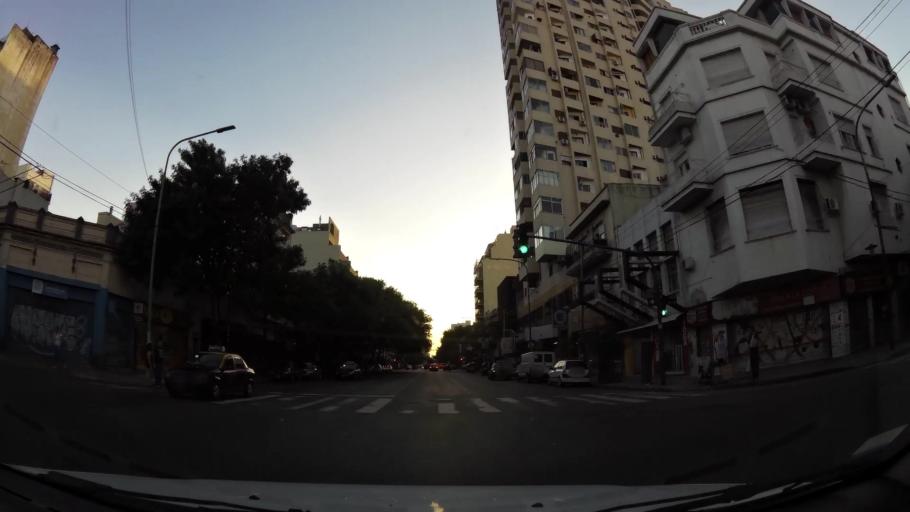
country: AR
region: Buenos Aires F.D.
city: Colegiales
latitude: -34.5978
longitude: -58.4356
